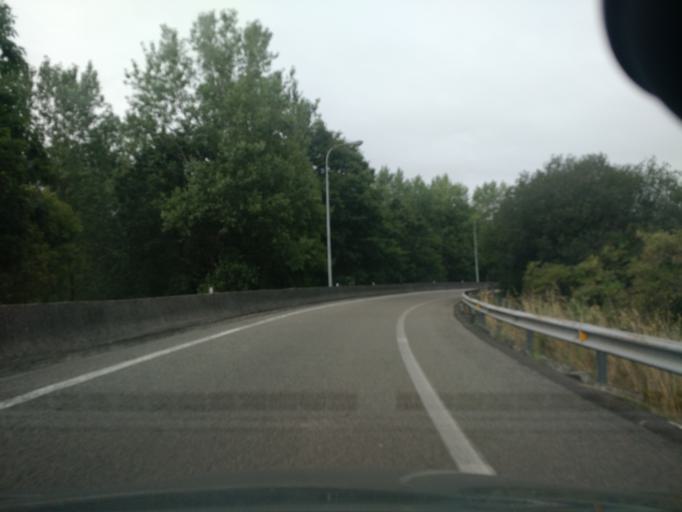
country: ES
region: Galicia
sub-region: Provincia da Coruna
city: Santiago de Compostela
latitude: 42.8902
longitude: -8.5048
